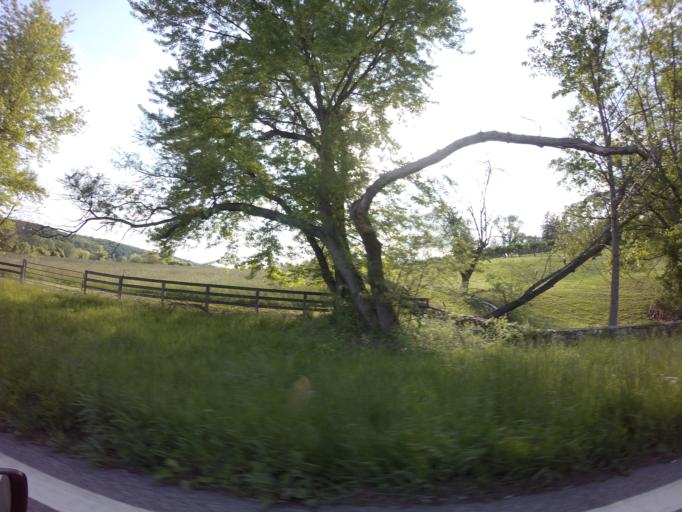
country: US
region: Maryland
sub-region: Baltimore County
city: Cockeysville
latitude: 39.4977
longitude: -76.7088
